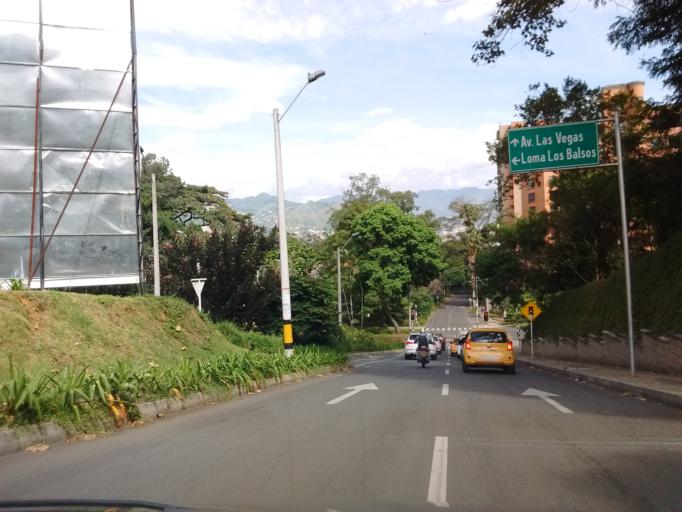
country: CO
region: Antioquia
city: Itagui
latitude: 6.2044
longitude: -75.5736
